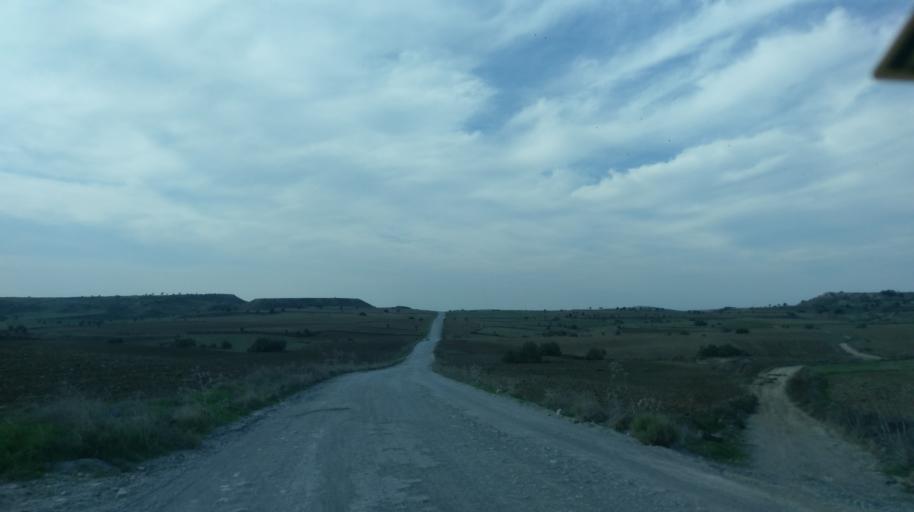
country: CY
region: Keryneia
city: Lapithos
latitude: 35.2832
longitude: 33.1634
